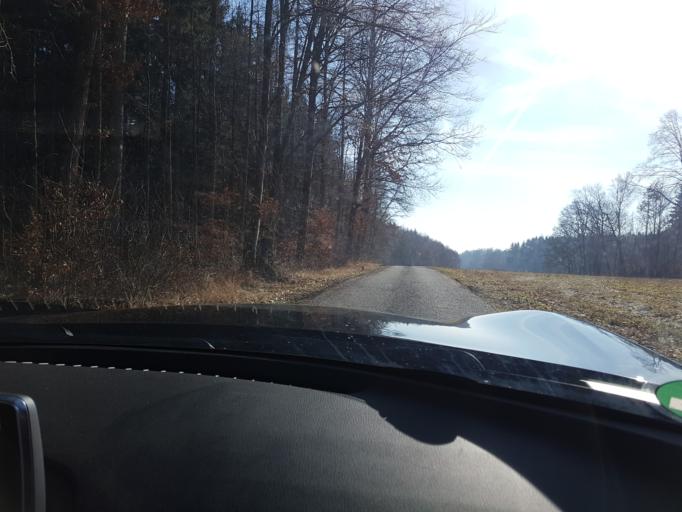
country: DE
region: Baden-Wuerttemberg
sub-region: Karlsruhe Region
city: Rosenberg
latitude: 49.4353
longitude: 9.4895
